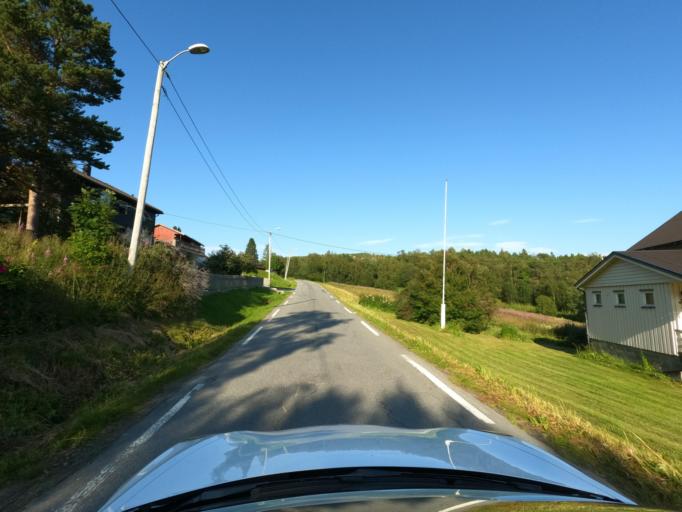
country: NO
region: Nordland
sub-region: Narvik
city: Narvik
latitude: 68.4719
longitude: 17.5048
